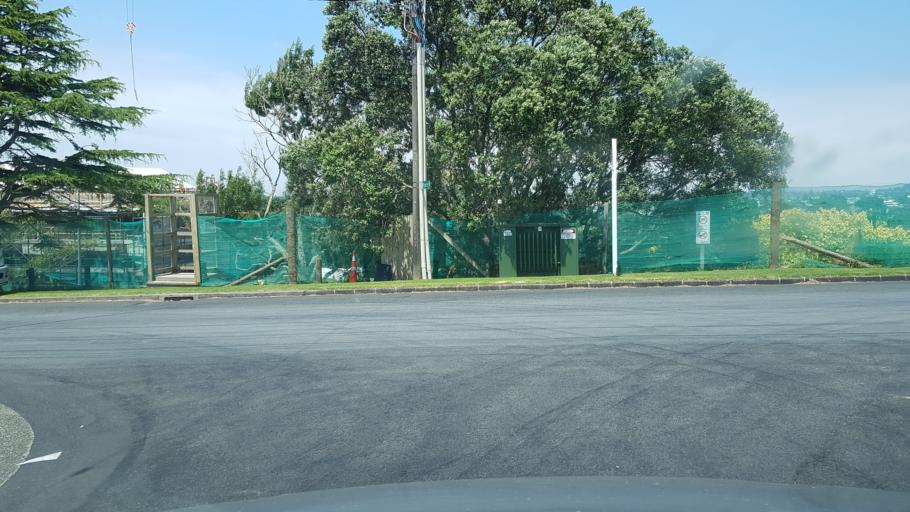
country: NZ
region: Auckland
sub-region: Auckland
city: North Shore
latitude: -36.8167
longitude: 174.7910
